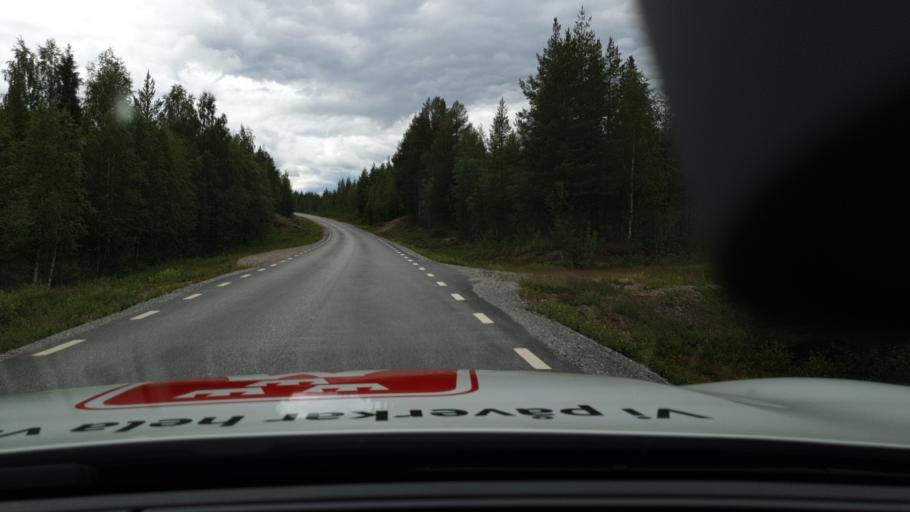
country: SE
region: Norrbotten
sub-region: Jokkmokks Kommun
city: Jokkmokk
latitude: 66.8524
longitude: 18.9482
